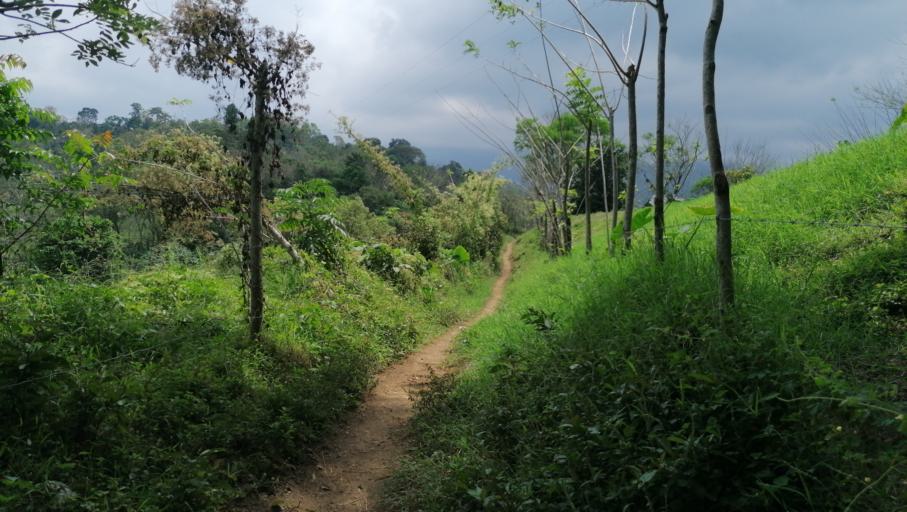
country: MX
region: Chiapas
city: Ocotepec
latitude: 17.2924
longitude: -93.2248
